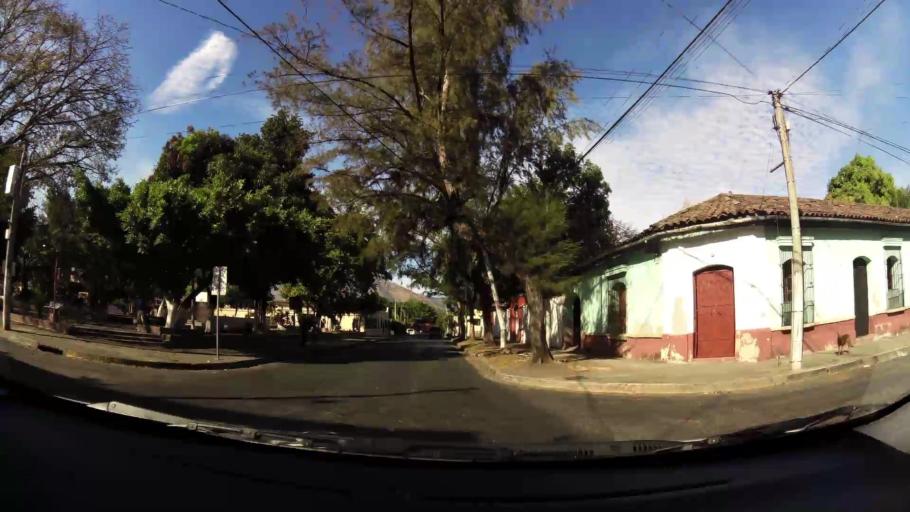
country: SV
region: Santa Ana
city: Santa Ana
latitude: 13.9942
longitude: -89.5638
